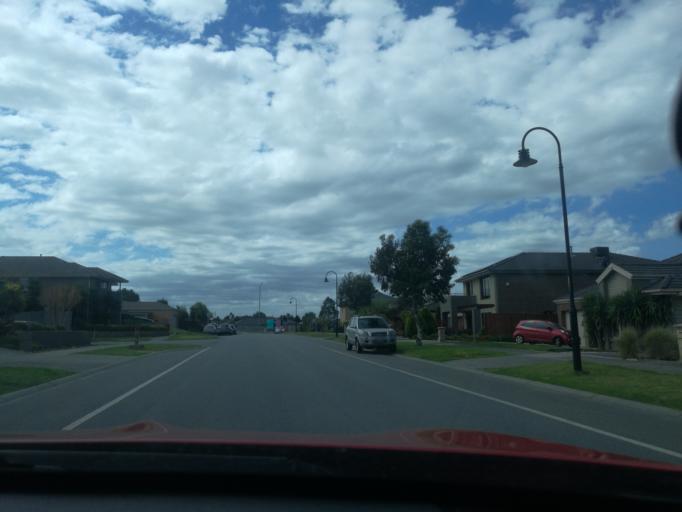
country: AU
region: Victoria
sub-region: Casey
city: Lynbrook
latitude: -38.0655
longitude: 145.2471
